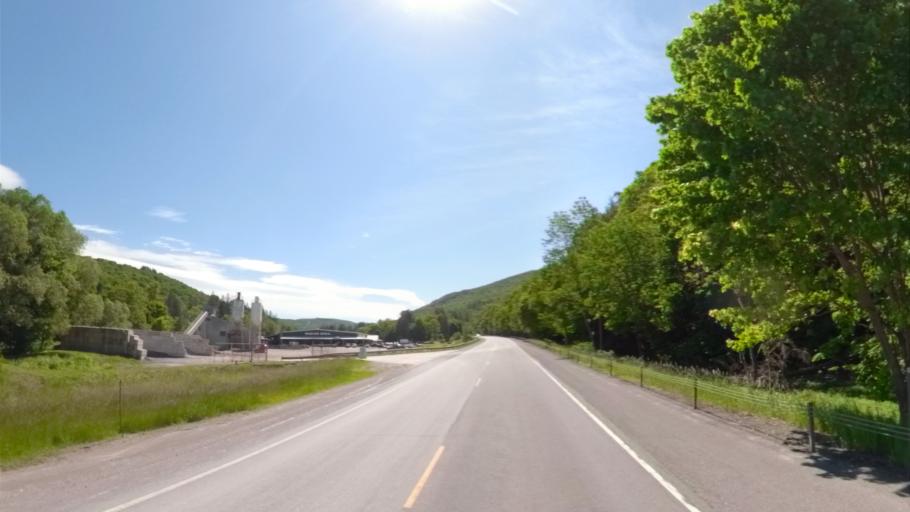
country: US
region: New York
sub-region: Delaware County
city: Stamford
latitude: 42.1555
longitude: -74.5471
